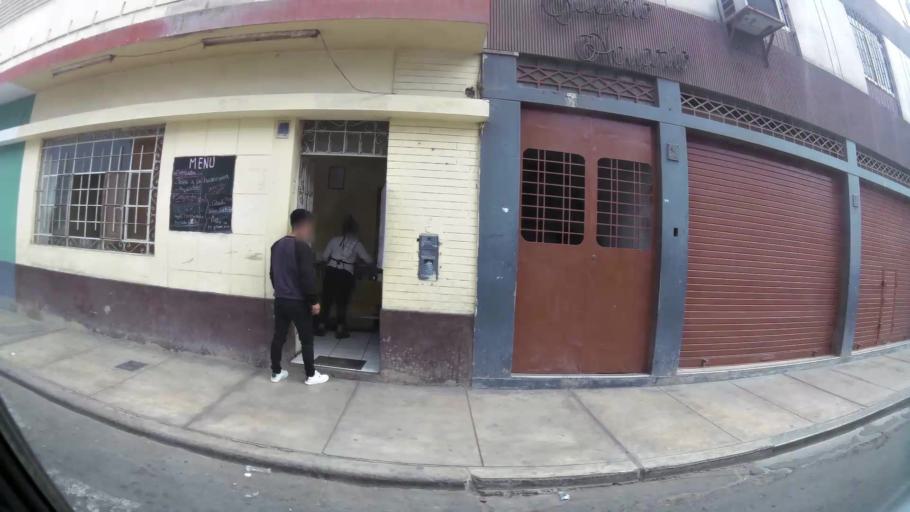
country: PE
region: La Libertad
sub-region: Provincia de Trujillo
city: Trujillo
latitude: -8.1107
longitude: -79.0226
